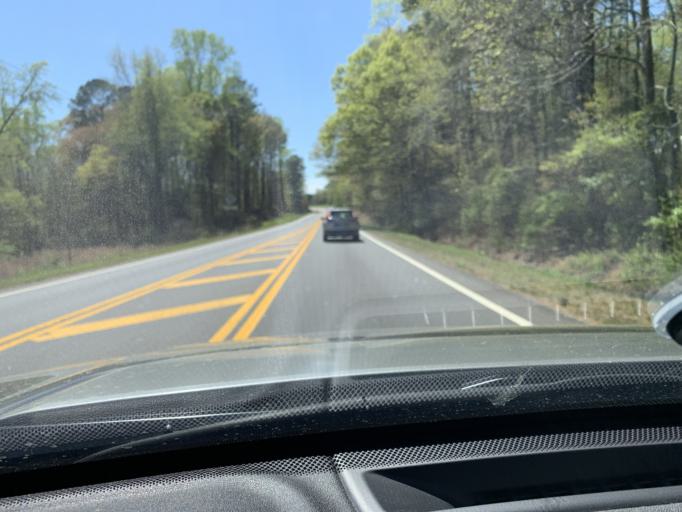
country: US
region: Georgia
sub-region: Fulton County
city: Milton
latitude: 34.1707
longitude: -84.2303
